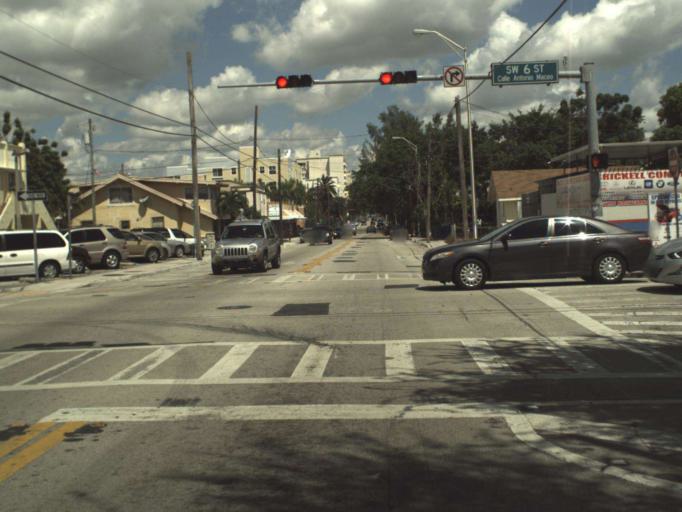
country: US
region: Florida
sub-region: Miami-Dade County
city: Miami
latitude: 25.7678
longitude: -80.2075
